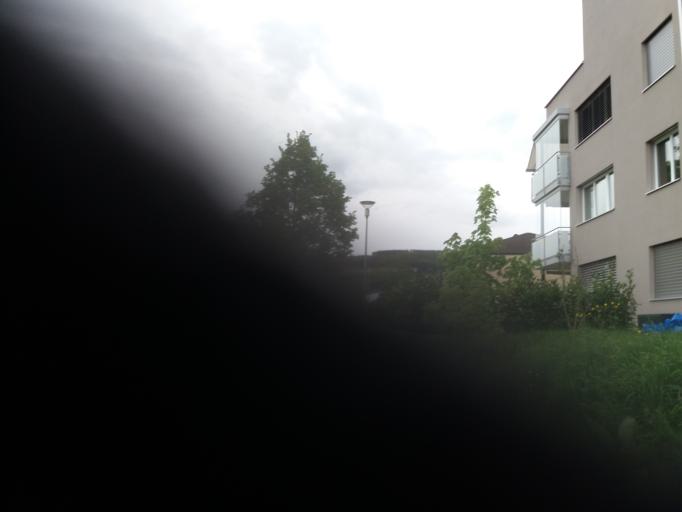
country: CH
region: Aargau
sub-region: Bezirk Laufenburg
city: Frick
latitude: 47.5116
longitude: 8.0197
